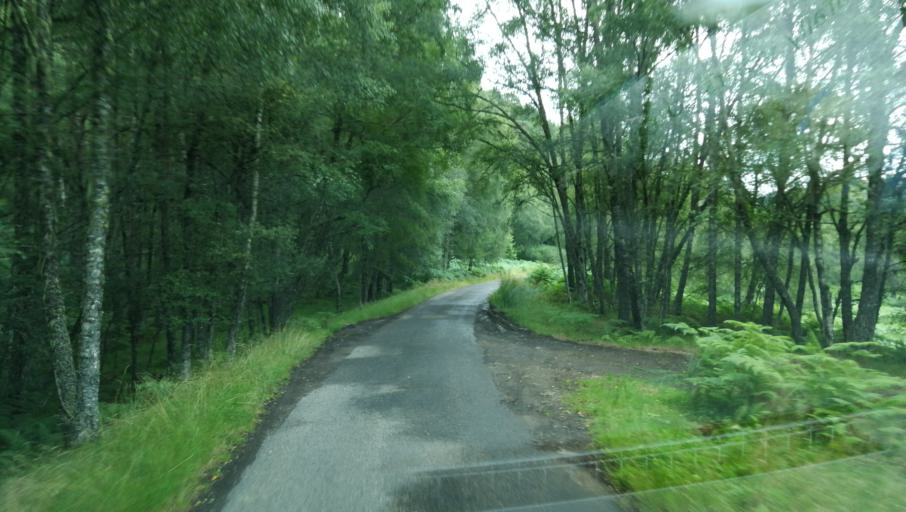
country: GB
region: Scotland
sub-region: Highland
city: Spean Bridge
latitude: 57.2946
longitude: -4.9155
